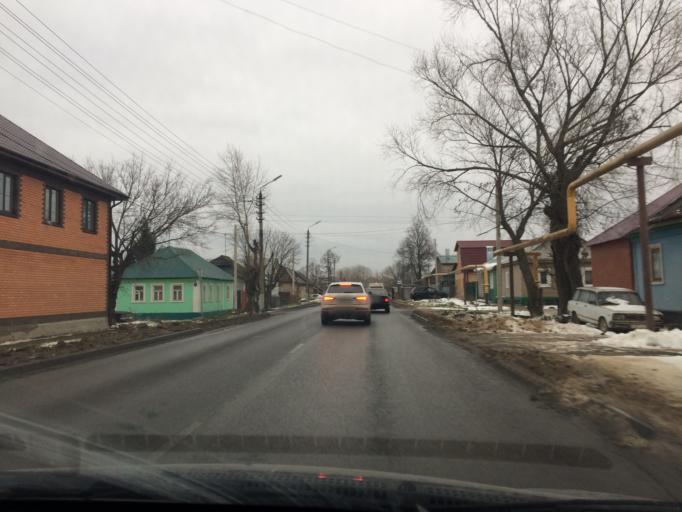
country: RU
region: Tula
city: Gorelki
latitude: 54.2386
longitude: 37.6428
